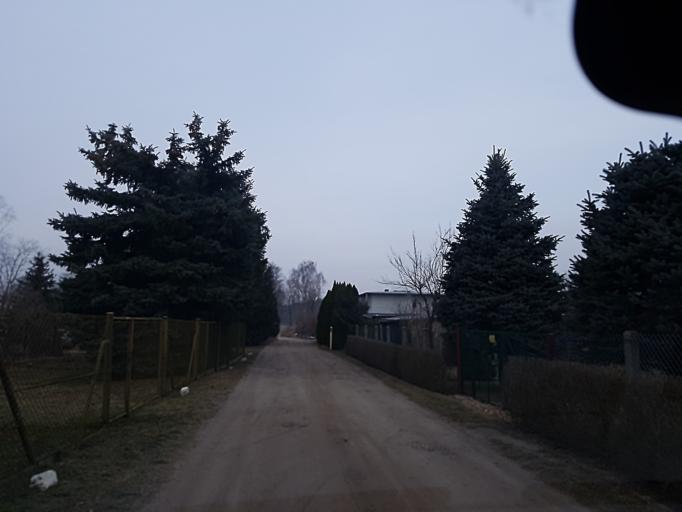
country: DE
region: Brandenburg
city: Finsterwalde
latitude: 51.6220
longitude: 13.6925
